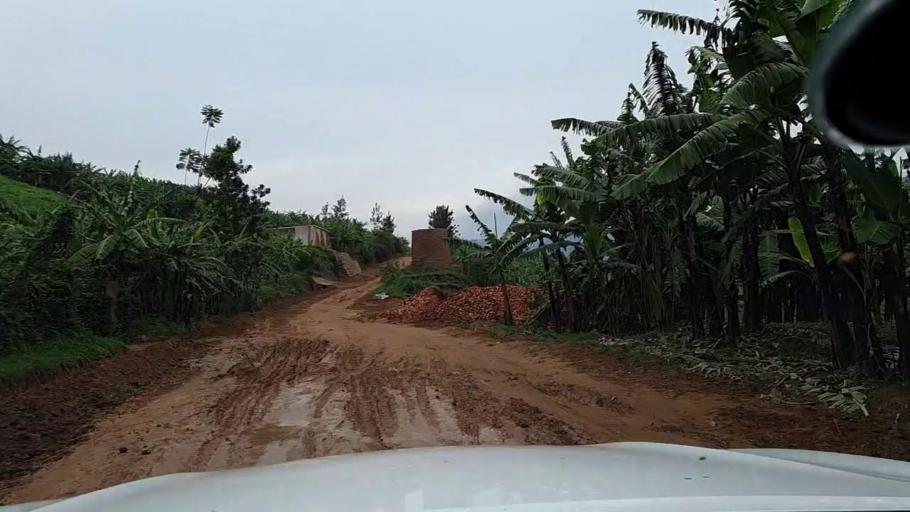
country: RW
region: Kigali
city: Kigali
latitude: -1.9474
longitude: 29.9894
